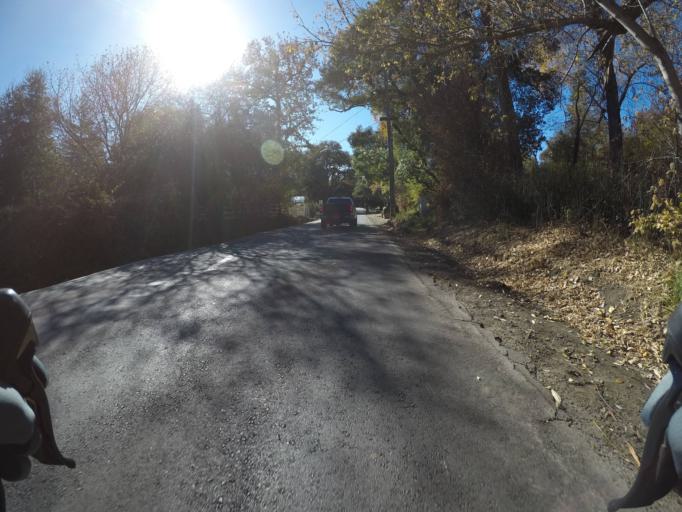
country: US
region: California
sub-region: Santa Cruz County
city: Mount Hermon
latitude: 37.0750
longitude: -122.0544
